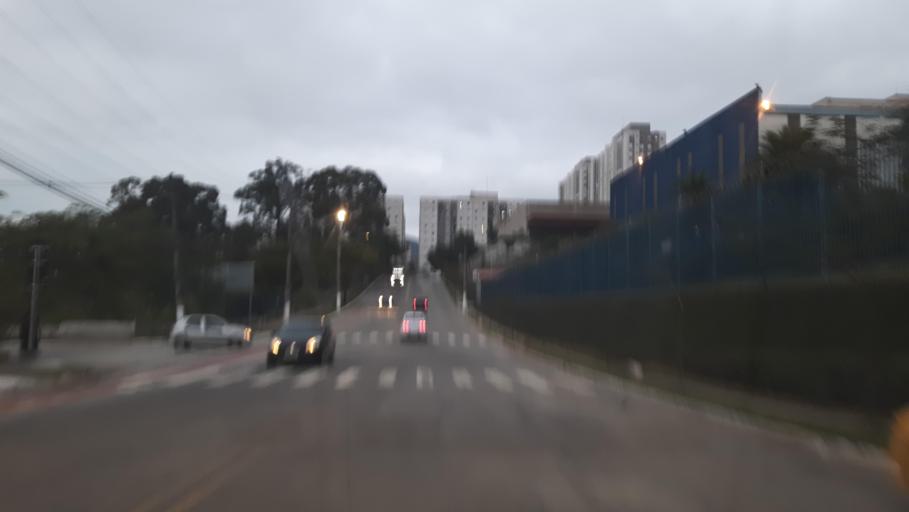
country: BR
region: Sao Paulo
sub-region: Caieiras
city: Caieiras
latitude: -23.4436
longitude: -46.7252
